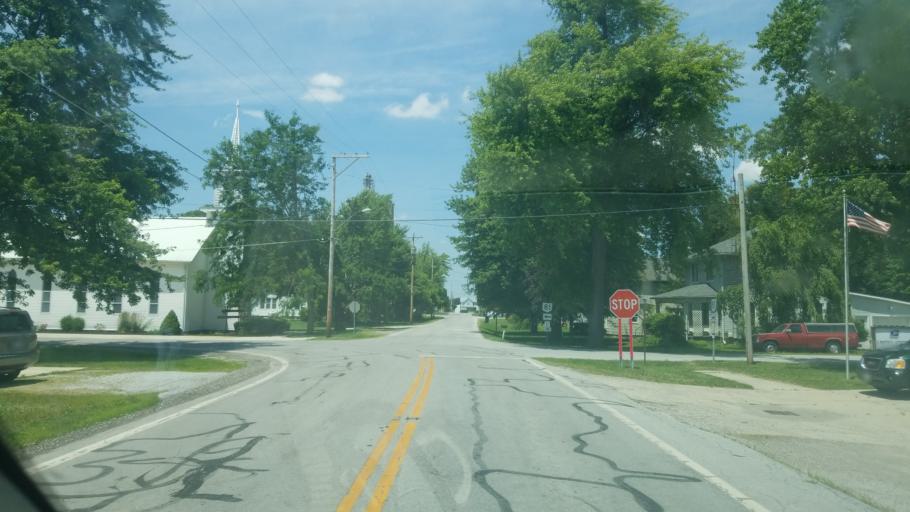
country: US
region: Ohio
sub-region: Hancock County
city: Arlington
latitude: 40.7819
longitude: -83.6927
